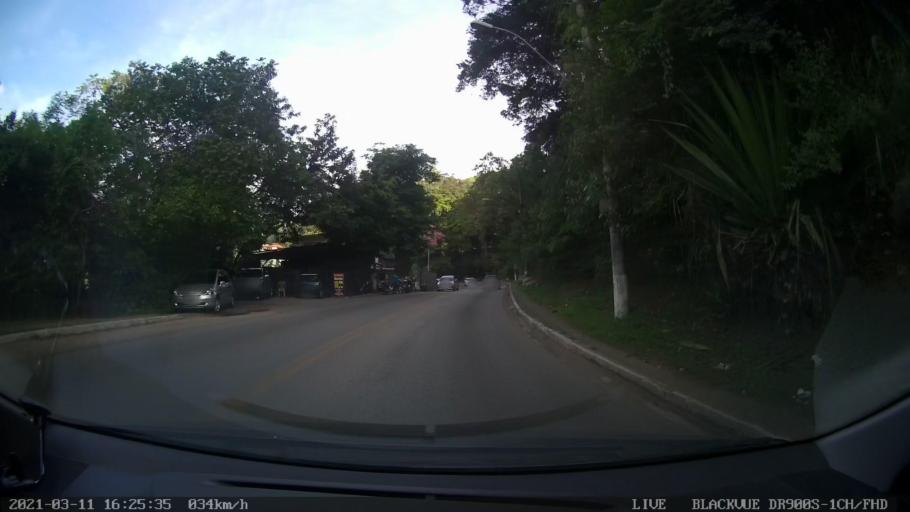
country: BR
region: Rio de Janeiro
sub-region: Petropolis
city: Petropolis
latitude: -22.4166
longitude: -43.1389
